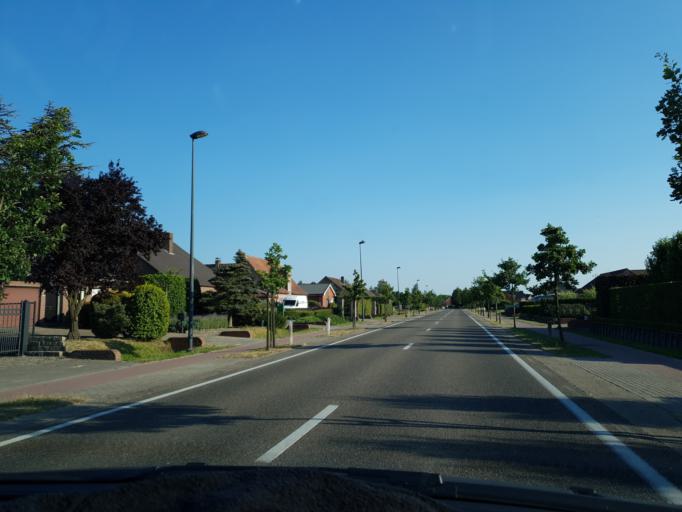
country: BE
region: Flanders
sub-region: Provincie Antwerpen
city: Oostmalle
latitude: 51.3136
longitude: 4.7377
